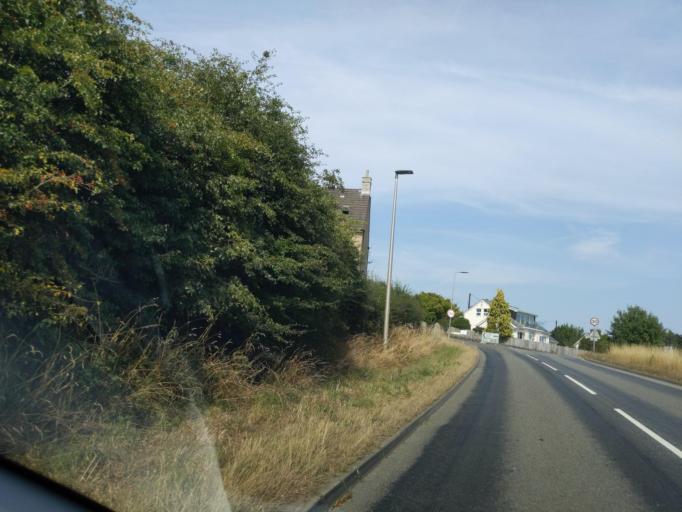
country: GB
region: England
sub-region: Devon
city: Winkleigh
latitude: 50.8538
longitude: -3.9418
